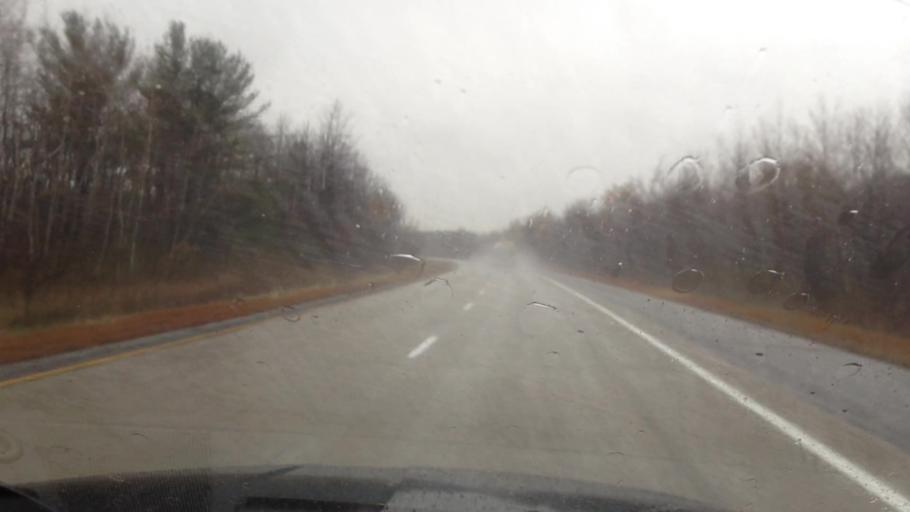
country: CA
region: Ontario
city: Hawkesbury
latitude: 45.4014
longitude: -74.7727
